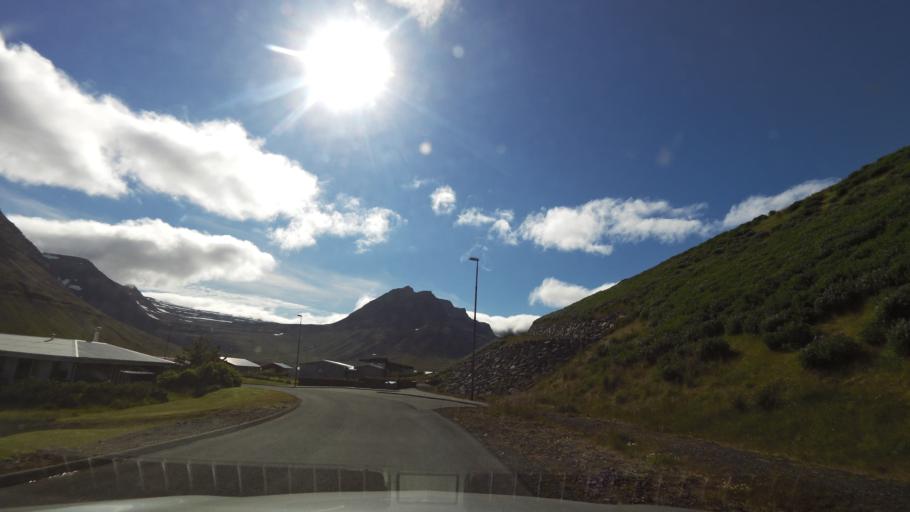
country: IS
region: Westfjords
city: Isafjoerdur
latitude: 66.1610
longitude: -23.2598
